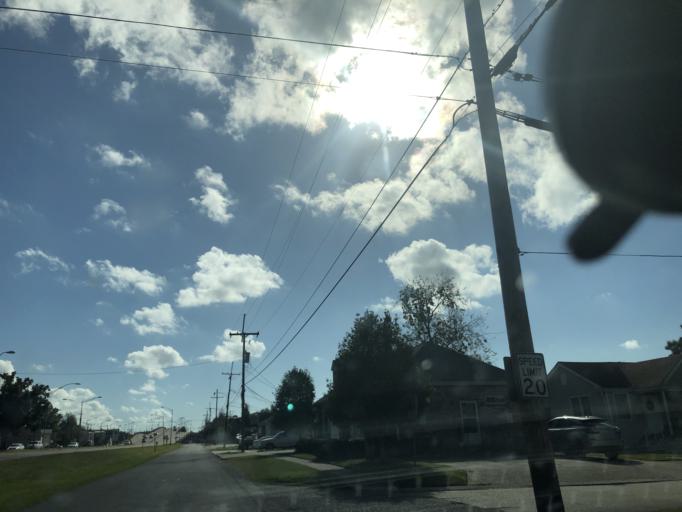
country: US
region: Louisiana
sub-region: Jefferson Parish
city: Metairie
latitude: 29.9806
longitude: -90.1563
